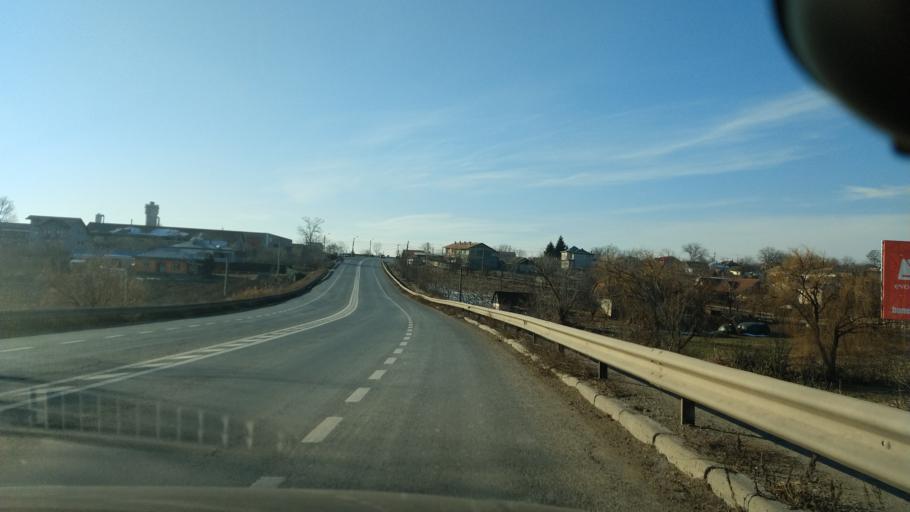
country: RO
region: Iasi
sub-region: Comuna Baltati
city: Baltati
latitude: 47.2199
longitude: 27.1218
